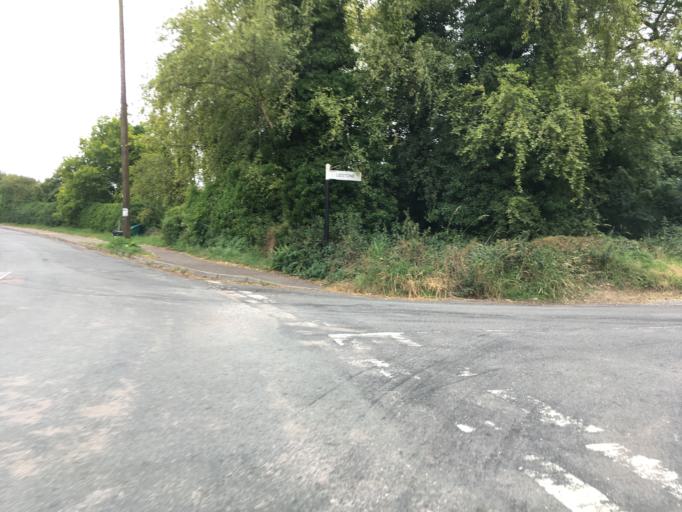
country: GB
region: England
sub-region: Oxfordshire
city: Charlbury
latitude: 51.9147
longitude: -1.4541
